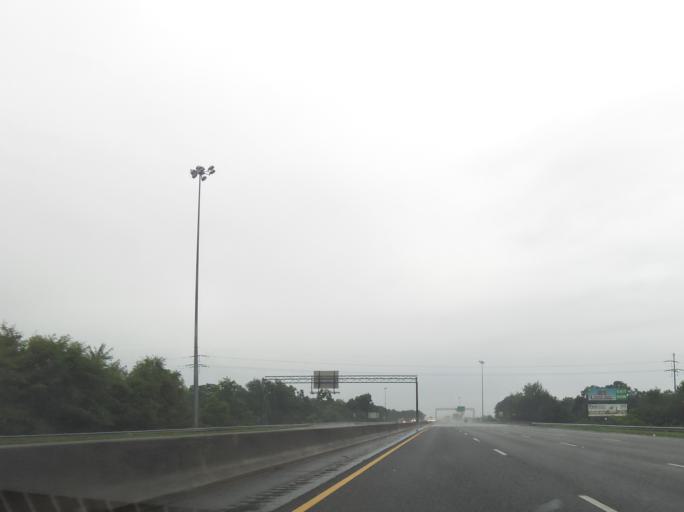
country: US
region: Georgia
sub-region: Tift County
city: Unionville
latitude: 31.4358
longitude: -83.5220
